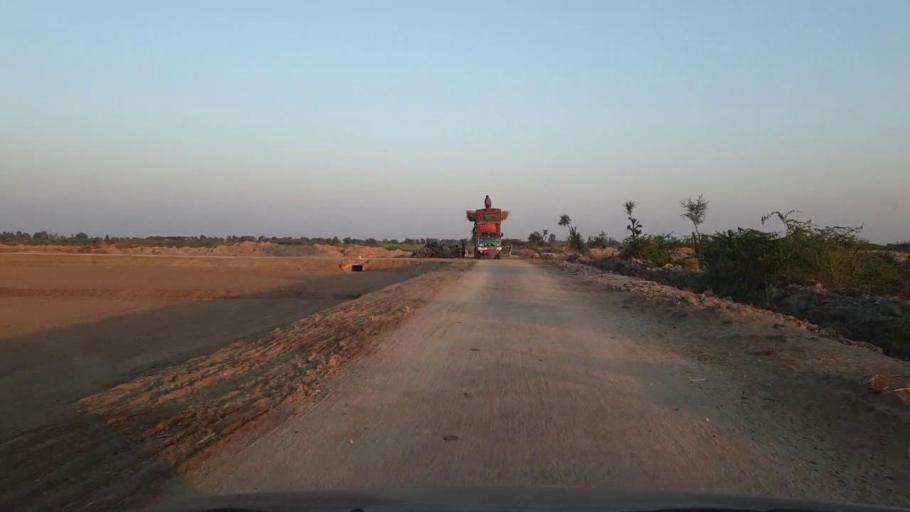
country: PK
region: Sindh
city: Digri
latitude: 25.1374
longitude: 69.2504
